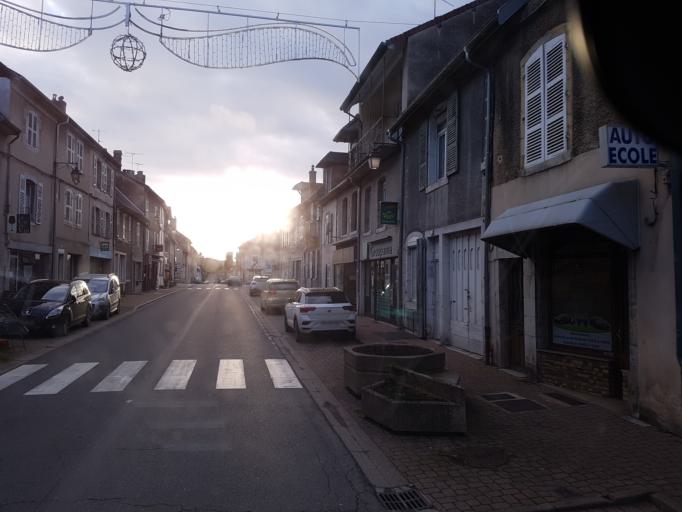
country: FR
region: Franche-Comte
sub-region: Departement du Jura
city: Poligny
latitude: 46.8343
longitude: 5.7082
